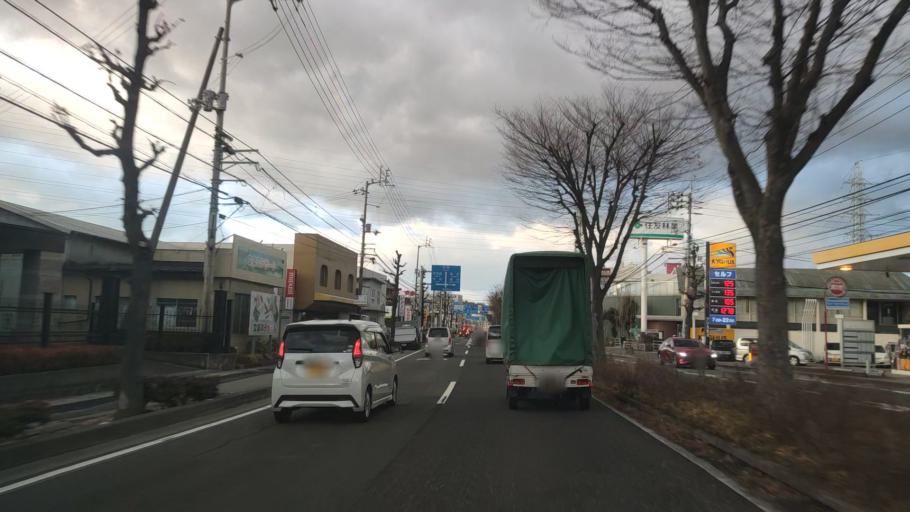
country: JP
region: Ehime
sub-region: Shikoku-chuo Shi
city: Matsuyama
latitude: 33.8191
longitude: 132.7769
